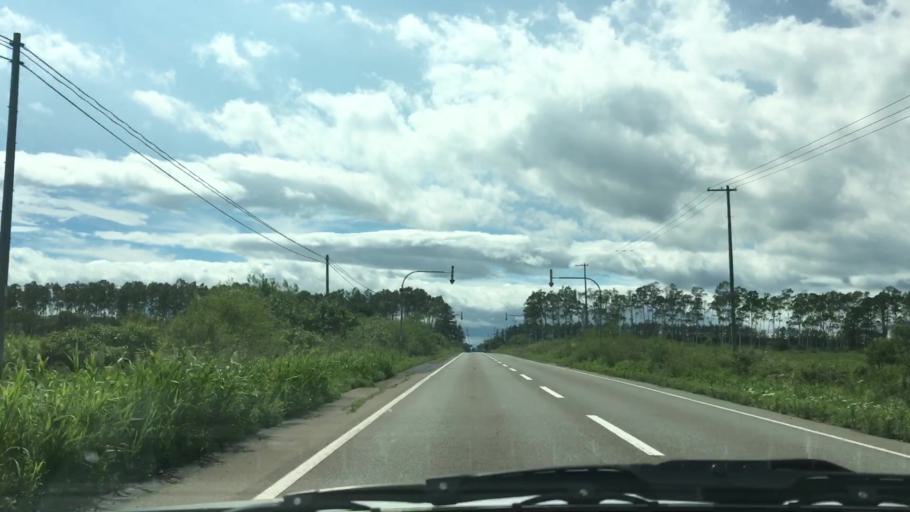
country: JP
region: Hokkaido
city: Otofuke
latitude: 43.2738
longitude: 143.4006
